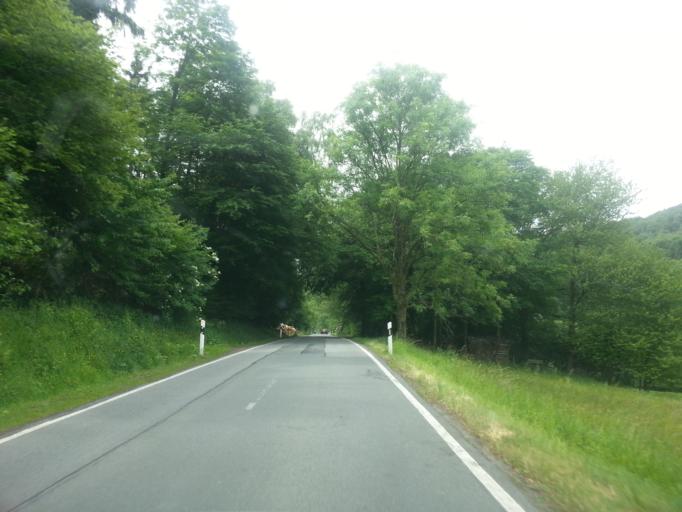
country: DE
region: Hesse
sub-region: Regierungsbezirk Darmstadt
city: Seeheim-Jugenheim
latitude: 49.7238
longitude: 8.6999
